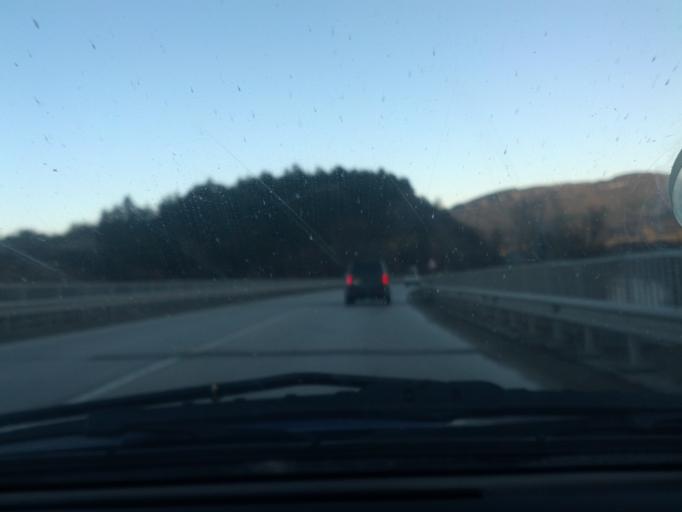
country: BG
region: Vratsa
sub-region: Obshtina Mezdra
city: Mezdra
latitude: 43.1383
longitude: 23.7027
